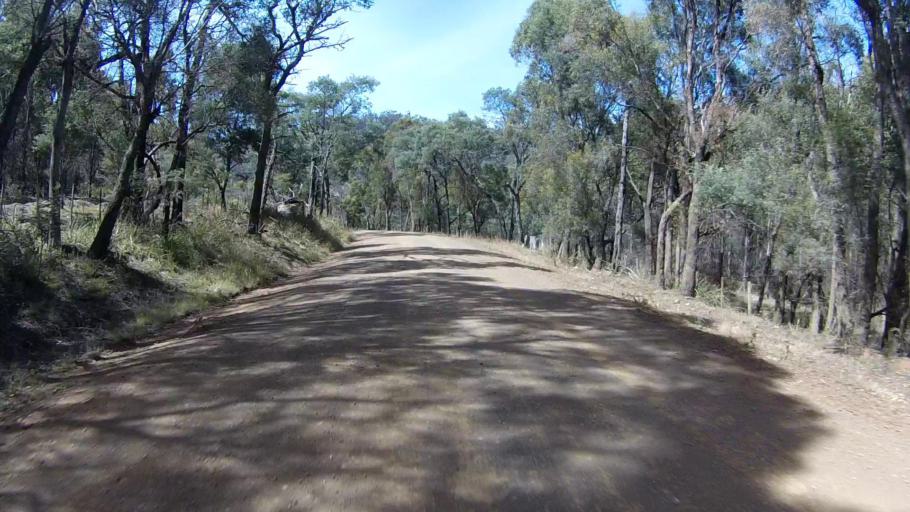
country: AU
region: Tasmania
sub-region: Sorell
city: Sorell
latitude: -42.6356
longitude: 147.7248
